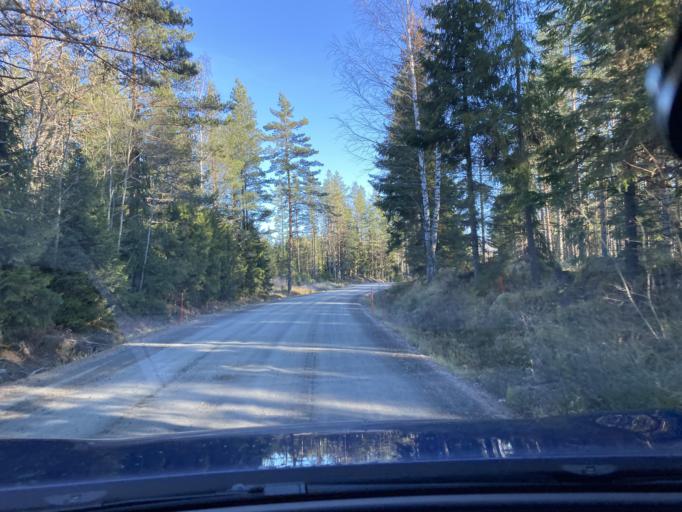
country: FI
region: Haeme
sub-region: Haemeenlinna
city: Kalvola
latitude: 60.9900
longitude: 24.0822
